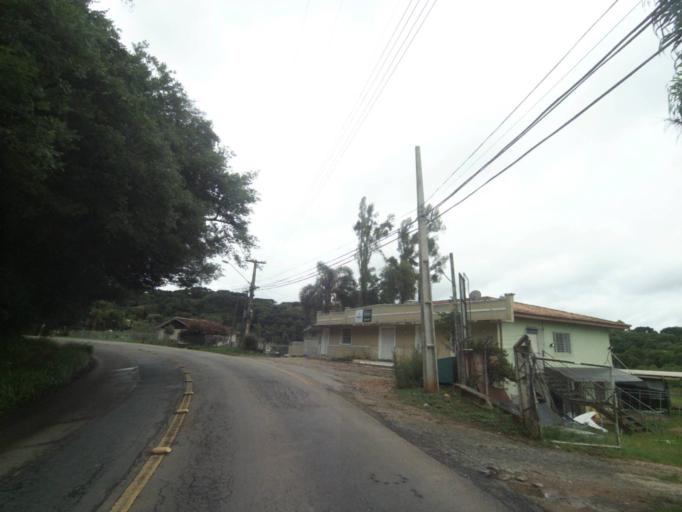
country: BR
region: Parana
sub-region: Curitiba
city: Curitiba
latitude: -25.4496
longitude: -49.3259
